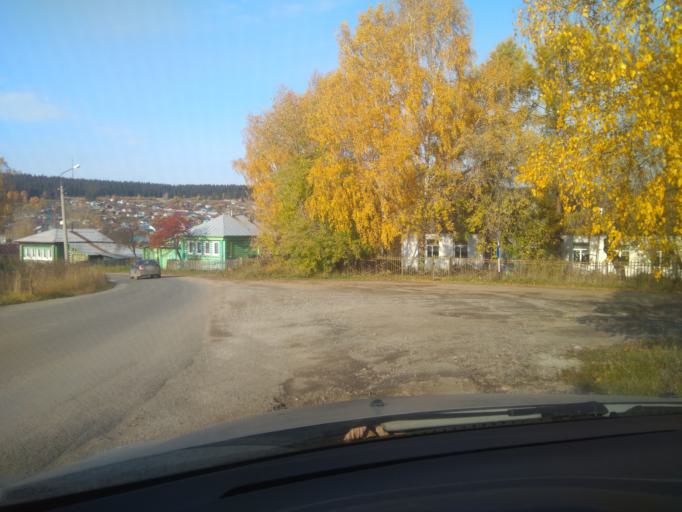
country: RU
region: Sverdlovsk
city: Nizhniye Sergi
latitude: 56.6768
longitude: 59.3347
